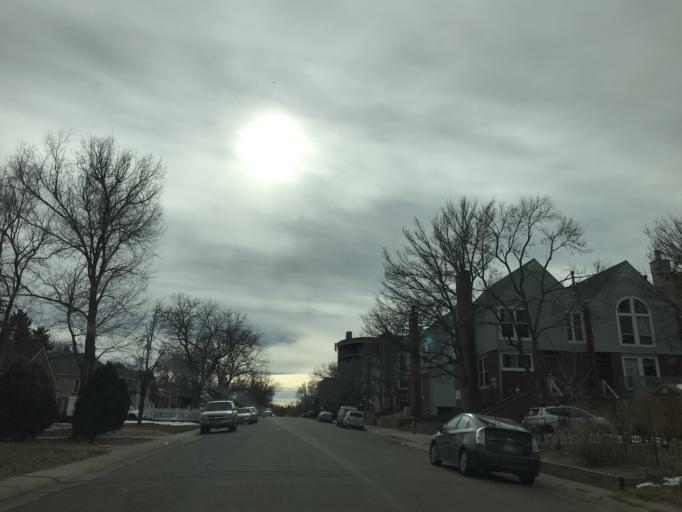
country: US
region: Colorado
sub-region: Arapahoe County
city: Glendale
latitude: 39.7331
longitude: -104.9184
